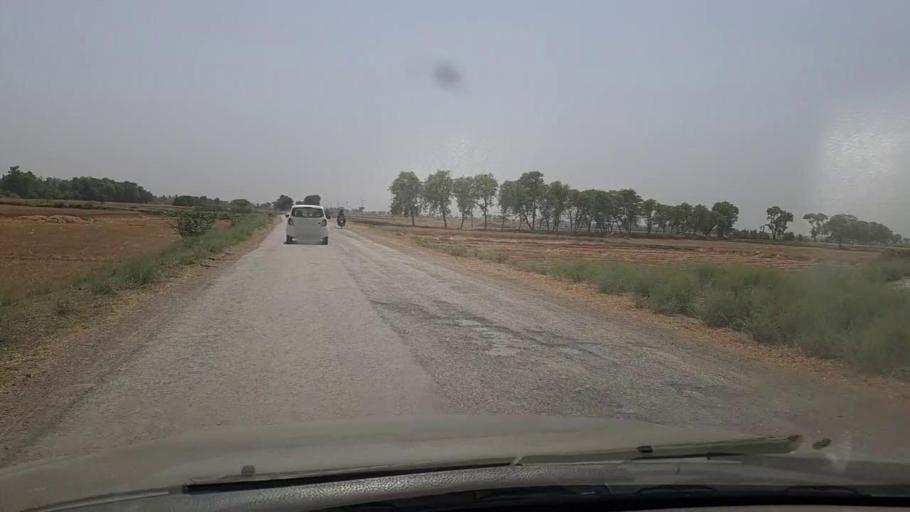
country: PK
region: Sindh
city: Miro Khan
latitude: 27.7239
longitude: 68.0701
